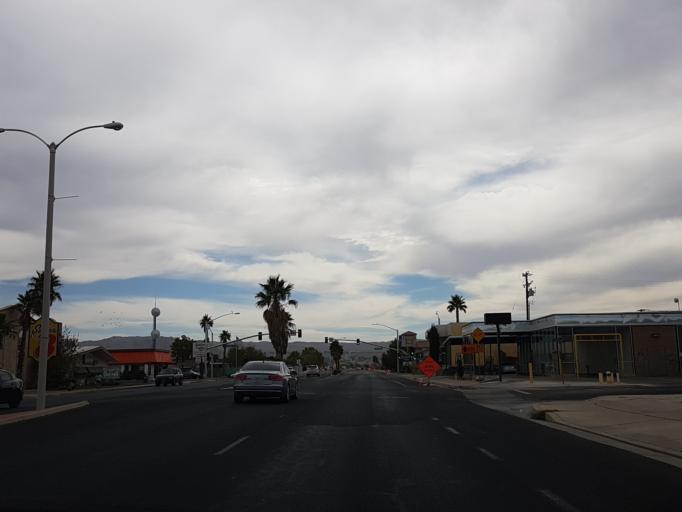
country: US
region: California
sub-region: Kern County
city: Ridgecrest
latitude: 35.6165
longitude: -117.6702
